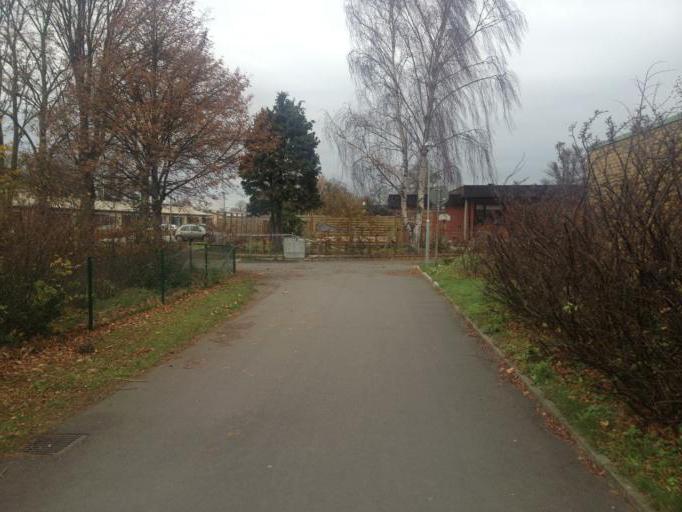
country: SE
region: Skane
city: Bjarred
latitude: 55.7218
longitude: 13.0235
